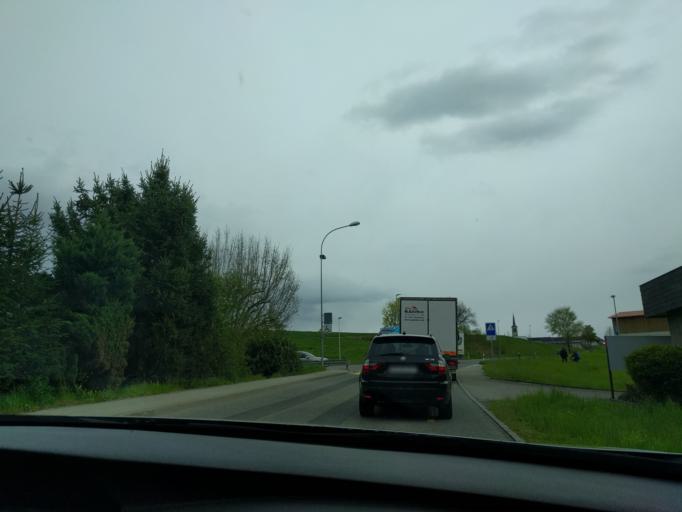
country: CH
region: Fribourg
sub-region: Sense District
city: Schmitten
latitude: 46.8609
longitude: 7.2502
